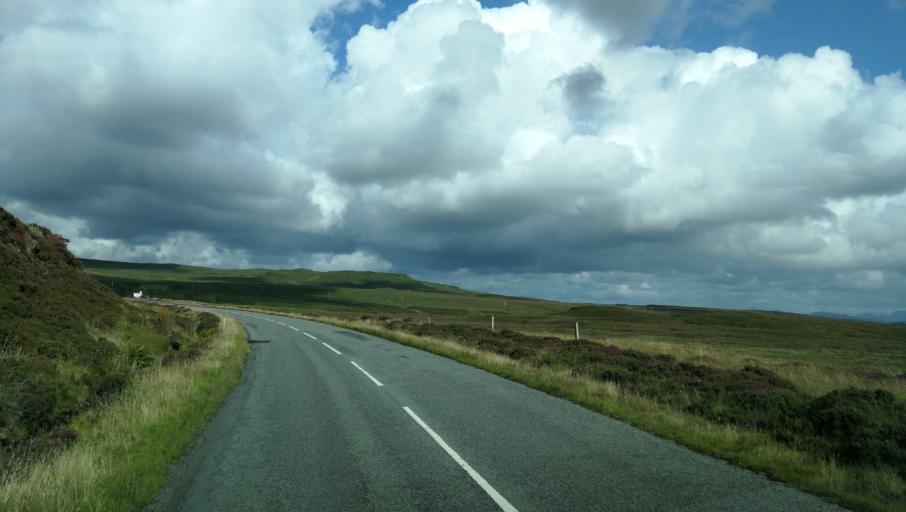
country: GB
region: Scotland
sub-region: Highland
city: Isle of Skye
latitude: 57.4388
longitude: -6.5572
